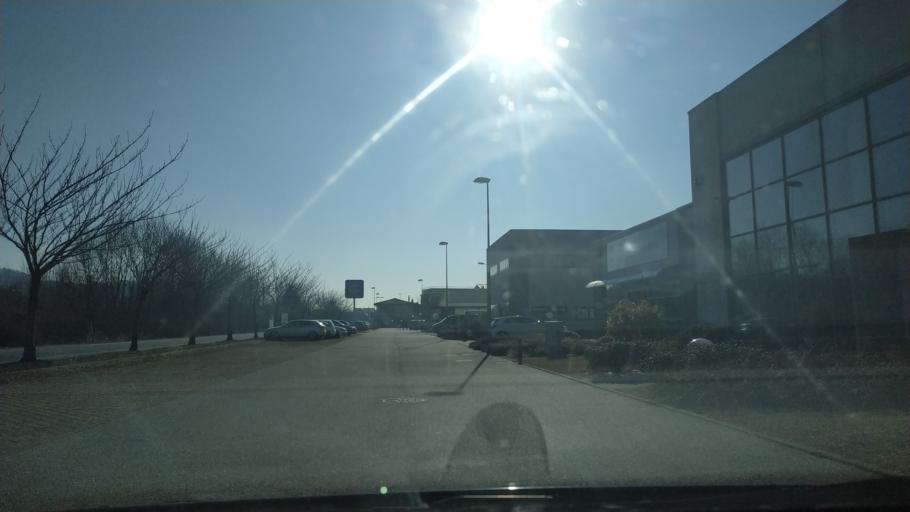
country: IT
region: Piedmont
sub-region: Provincia di Torino
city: Montalto Dora
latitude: 45.4986
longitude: 7.8579
